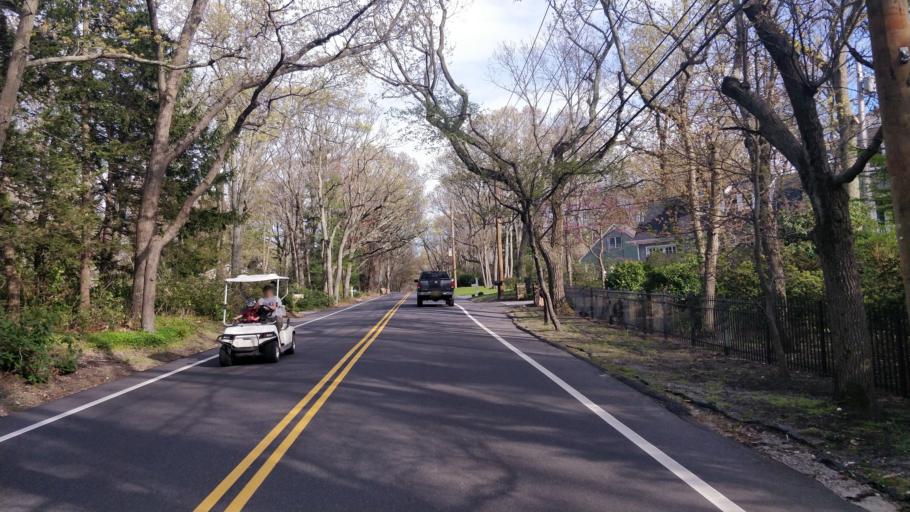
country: US
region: New York
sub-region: Suffolk County
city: Stony Brook
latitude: 40.9414
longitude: -73.1331
